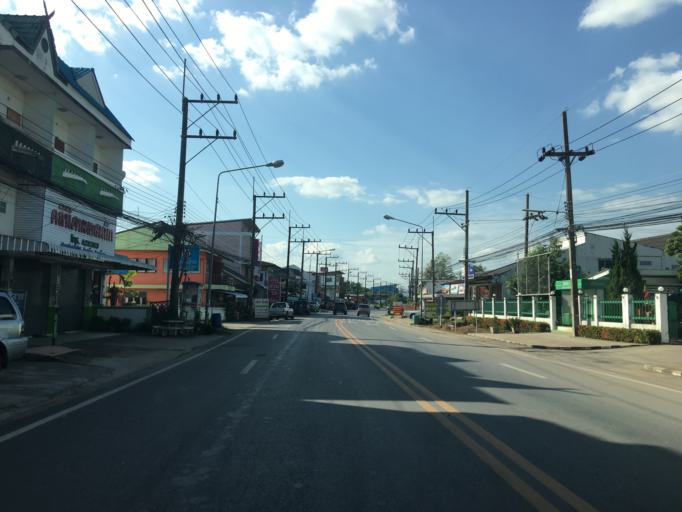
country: TH
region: Phayao
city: Chun
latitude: 19.3417
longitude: 100.1229
